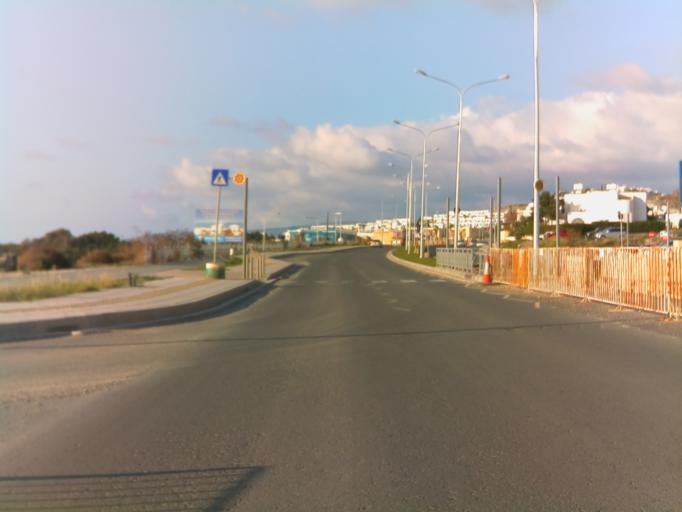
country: CY
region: Pafos
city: Chlorakas
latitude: 34.7802
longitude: 32.4060
